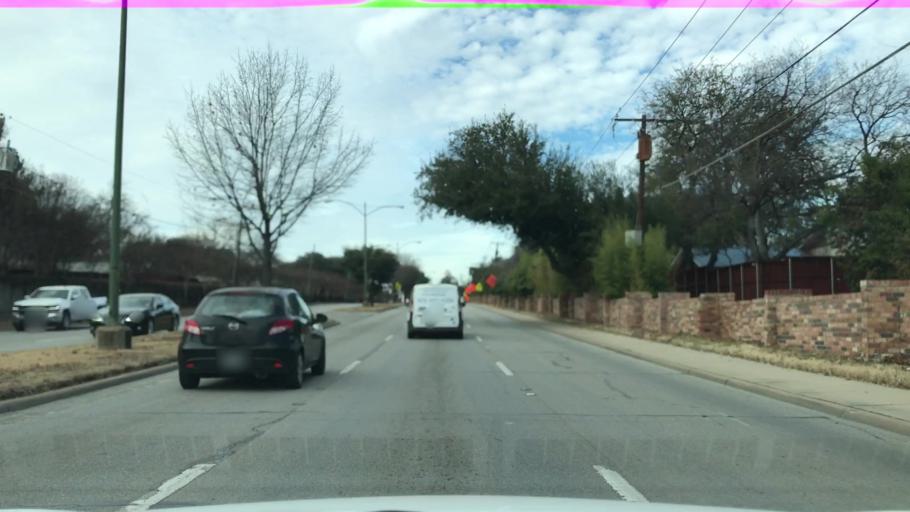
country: US
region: Texas
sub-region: Dallas County
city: University Park
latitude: 32.8801
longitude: -96.7802
